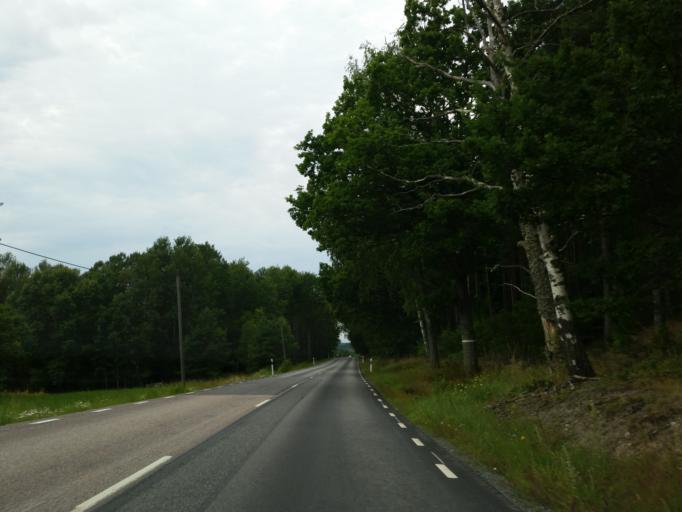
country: SE
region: Stockholm
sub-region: Nykvarns Kommun
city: Nykvarn
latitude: 59.1891
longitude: 17.4776
